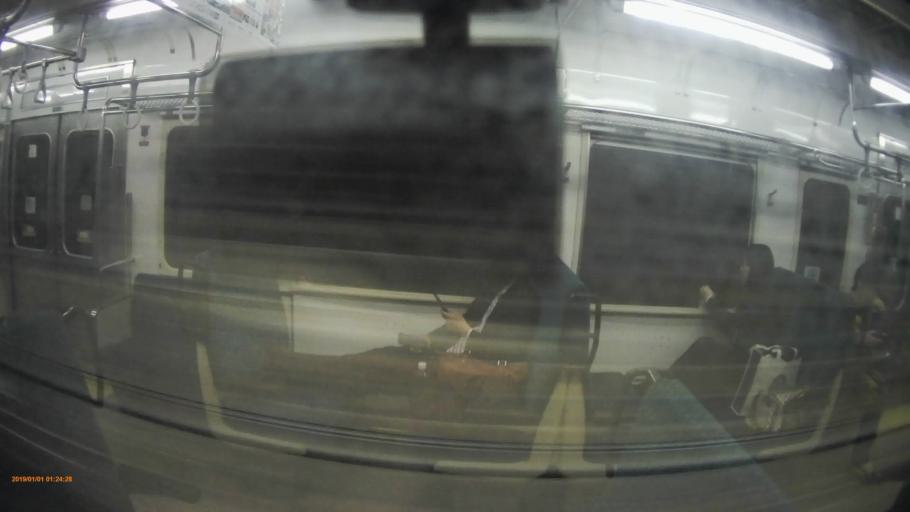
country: JP
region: Yamanashi
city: Enzan
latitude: 35.6859
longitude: 138.7407
